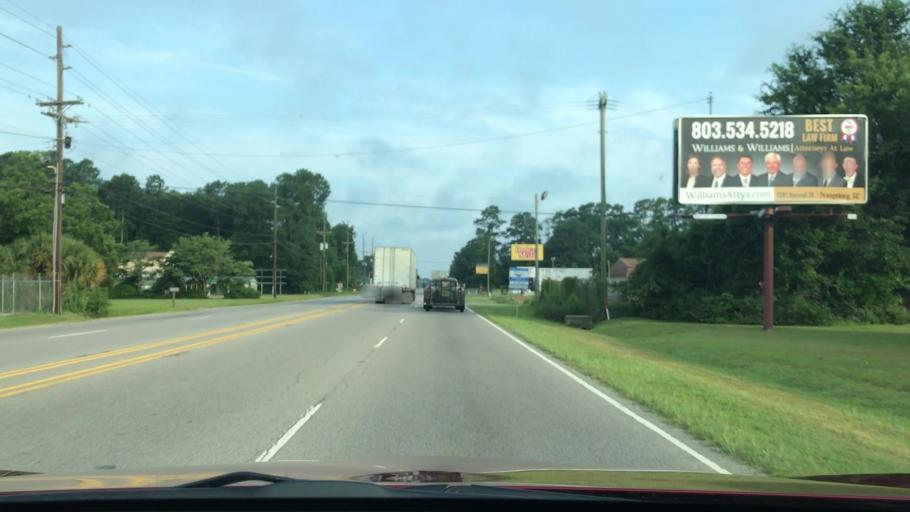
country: US
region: South Carolina
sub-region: Orangeburg County
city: Wilkinson Heights
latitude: 33.4784
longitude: -80.8185
